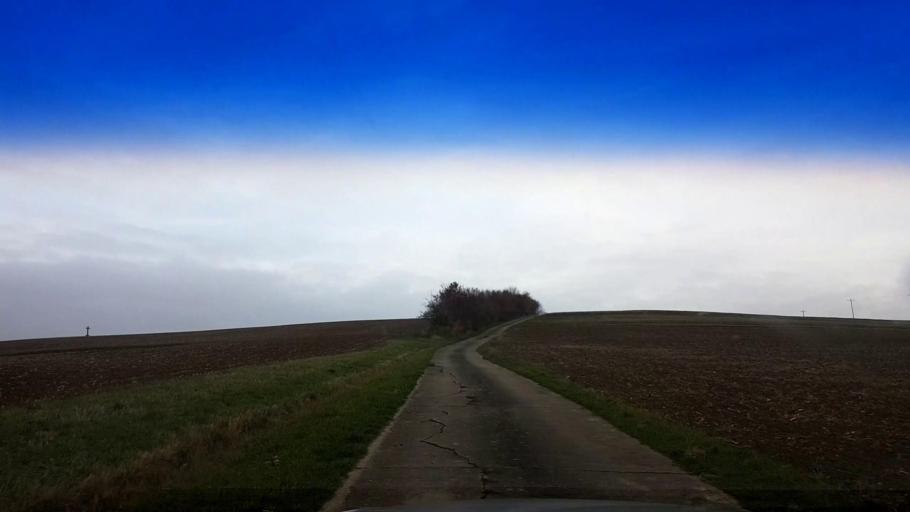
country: DE
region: Bavaria
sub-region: Upper Franconia
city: Zapfendorf
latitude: 50.0067
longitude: 10.9858
